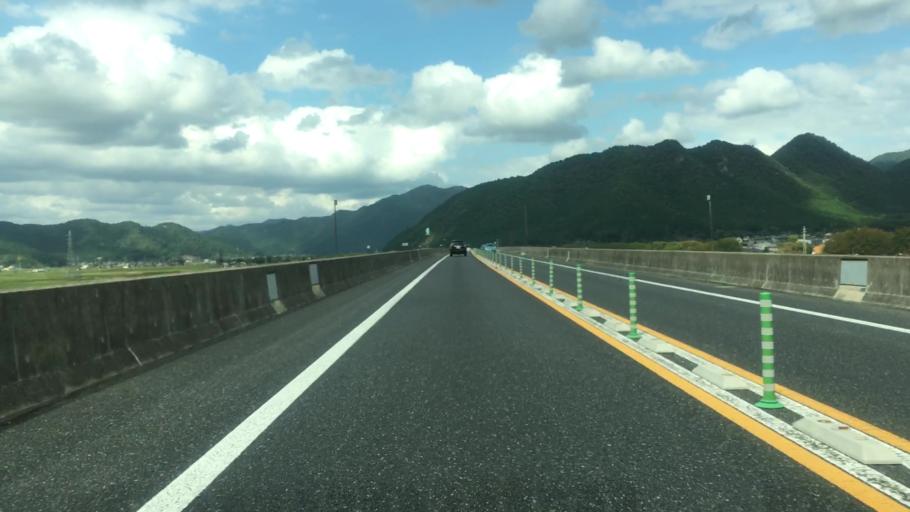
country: JP
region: Kyoto
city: Fukuchiyama
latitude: 35.1972
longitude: 135.0425
